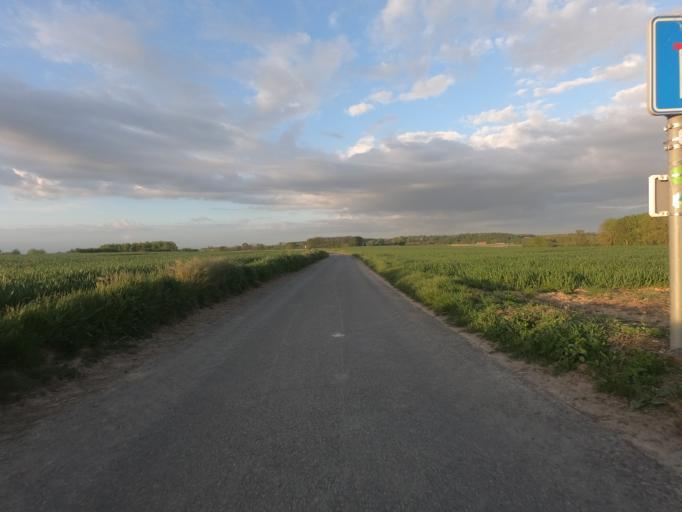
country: BE
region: Flanders
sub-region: Provincie Vlaams-Brabant
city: Lennik
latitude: 50.7895
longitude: 4.1655
